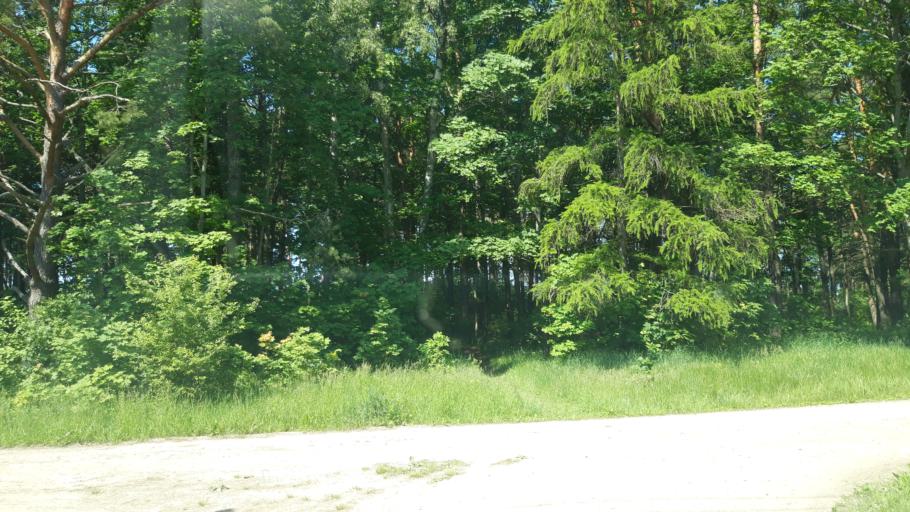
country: LV
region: Saulkrastu
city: Saulkrasti
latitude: 57.2581
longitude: 24.4105
